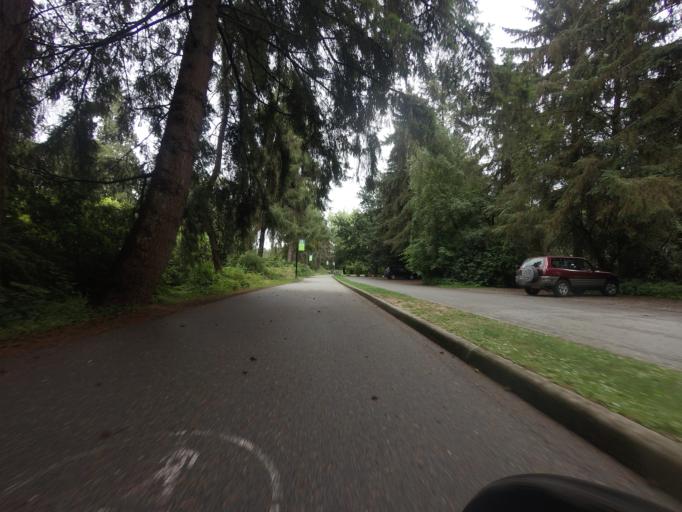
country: CA
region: British Columbia
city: West End
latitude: 49.3228
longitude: -123.1429
